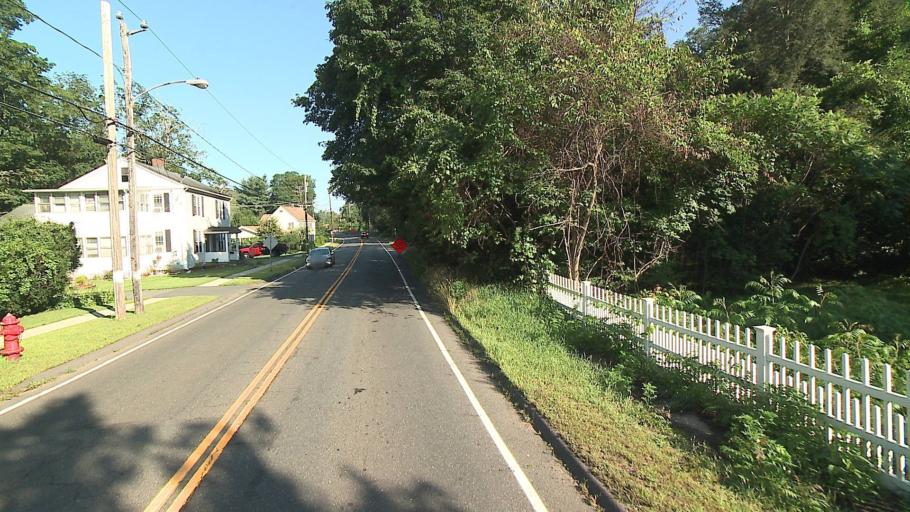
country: US
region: Connecticut
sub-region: Hartford County
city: Collinsville
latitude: 41.7631
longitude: -72.8936
